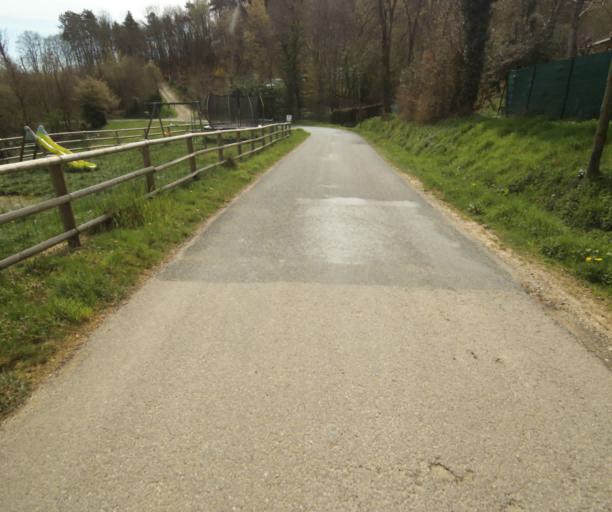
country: FR
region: Limousin
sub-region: Departement de la Correze
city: Naves
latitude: 45.2999
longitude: 1.7650
